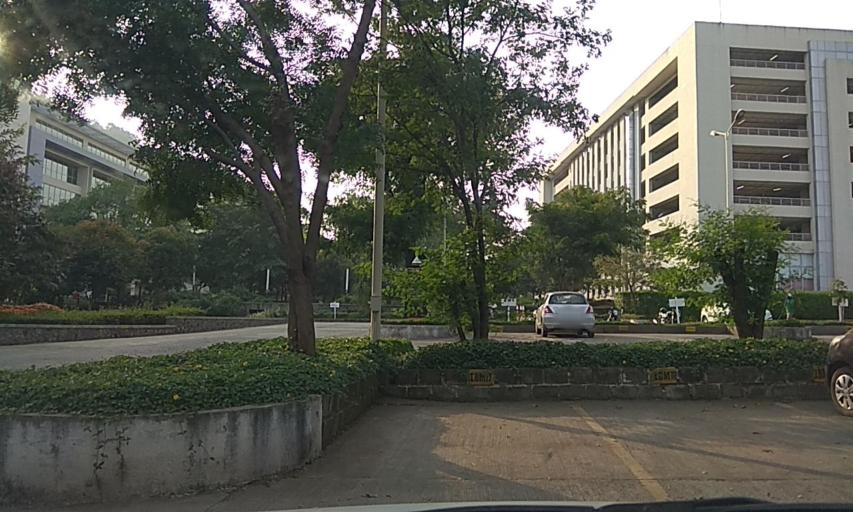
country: IN
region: Maharashtra
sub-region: Pune Division
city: Pimpri
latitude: 18.6043
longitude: 73.7165
